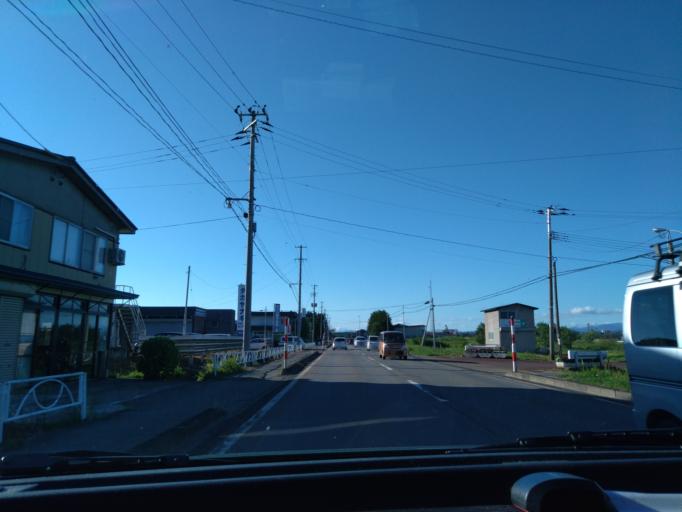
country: JP
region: Akita
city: Omagari
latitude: 39.4321
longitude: 140.4850
